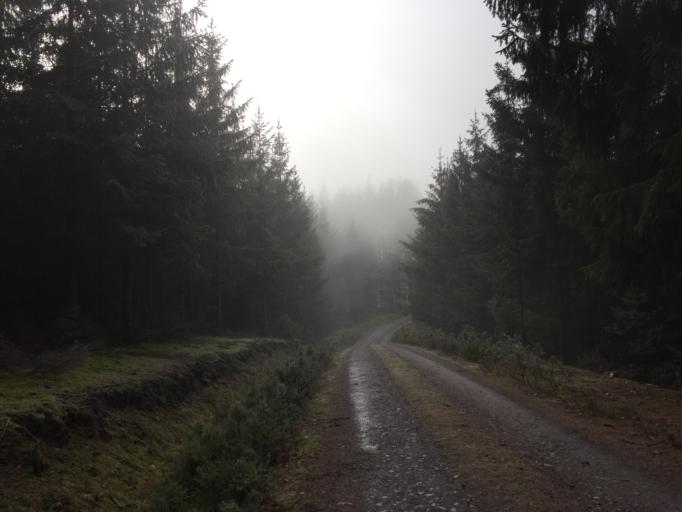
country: DE
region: Thuringia
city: Orlamunde
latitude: 50.7411
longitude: 11.5079
